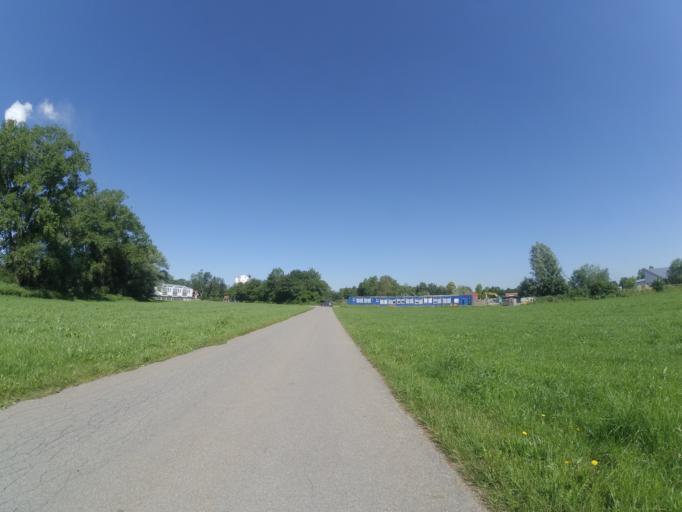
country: DE
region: Baden-Wuerttemberg
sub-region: Tuebingen Region
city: Leutkirch im Allgau
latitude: 47.8332
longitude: 10.0160
